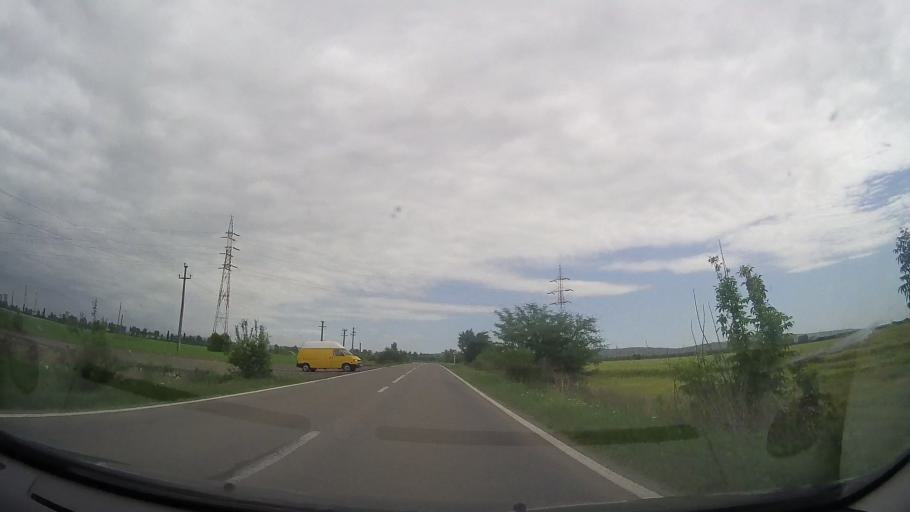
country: RO
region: Prahova
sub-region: Comuna Berceni
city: Berceni
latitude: 44.9306
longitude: 26.1038
